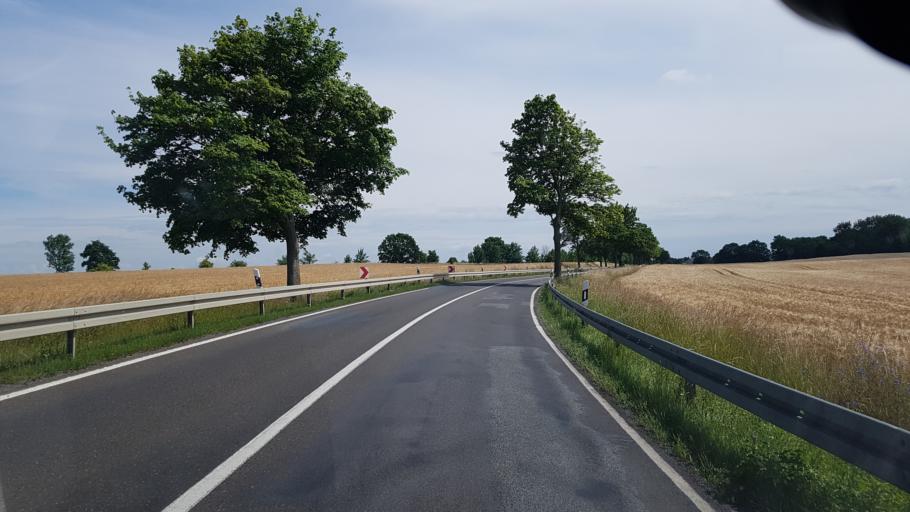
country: DE
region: Mecklenburg-Vorpommern
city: Strasburg
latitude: 53.3937
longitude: 13.7693
